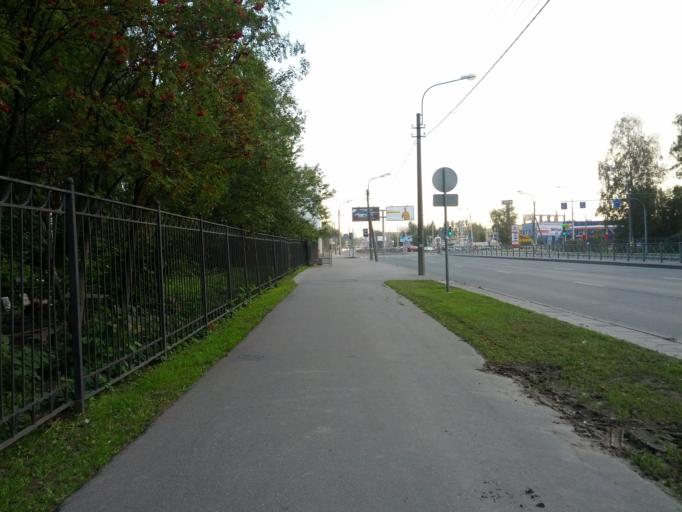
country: RU
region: St.-Petersburg
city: Krasnogvargeisky
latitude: 59.9490
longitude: 30.4368
